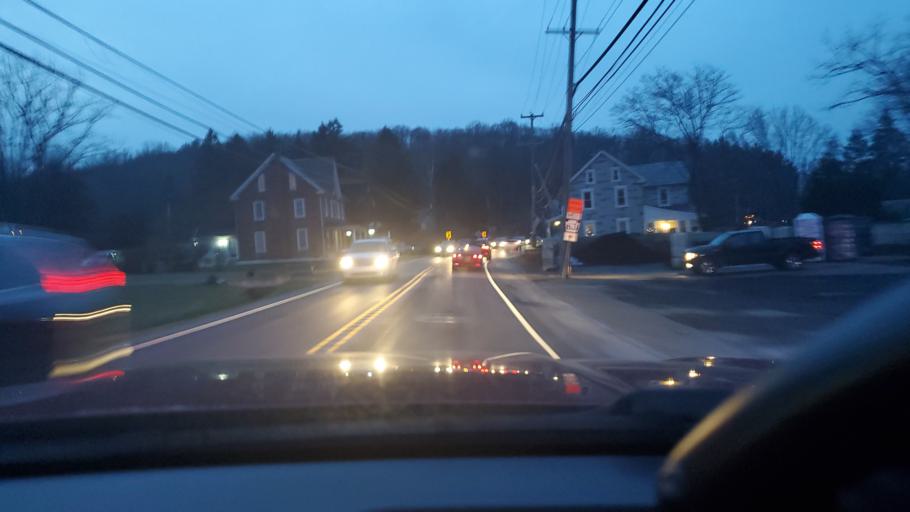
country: US
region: Pennsylvania
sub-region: Montgomery County
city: Schwenksville
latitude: 40.2688
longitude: -75.4695
